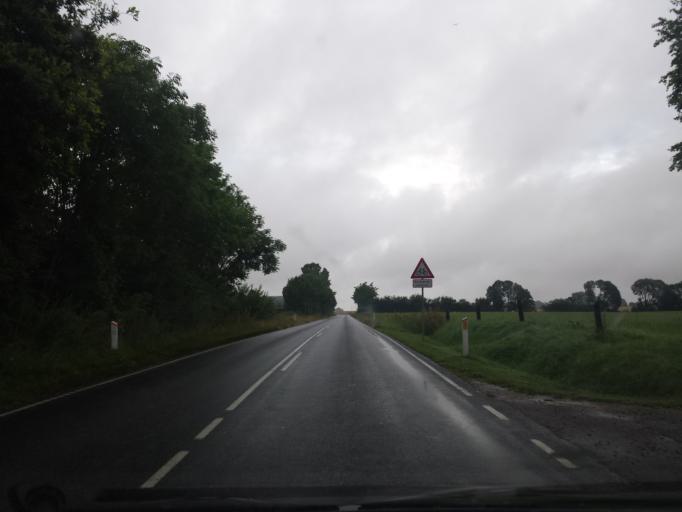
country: DK
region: South Denmark
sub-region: Sonderborg Kommune
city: Grasten
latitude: 54.9413
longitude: 9.6288
